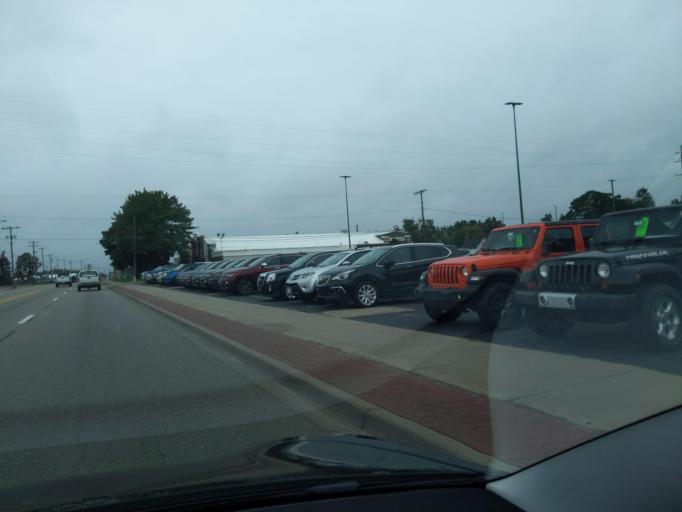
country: US
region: Michigan
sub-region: Wexford County
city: Cadillac
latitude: 44.2641
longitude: -85.4059
